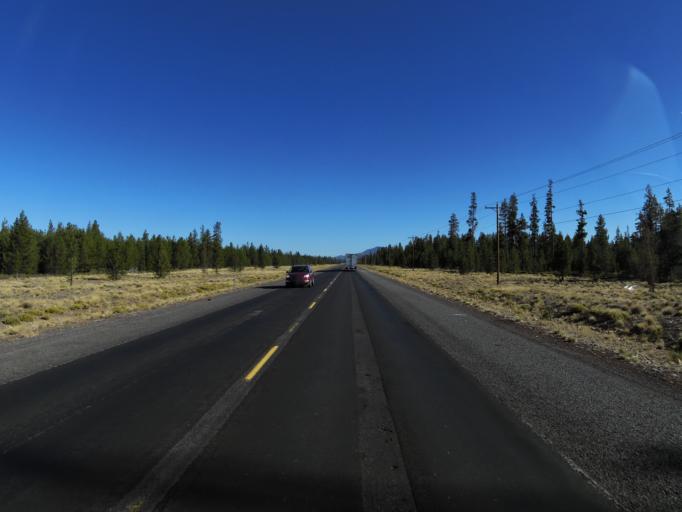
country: US
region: Oregon
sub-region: Deschutes County
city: La Pine
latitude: 43.1481
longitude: -121.7972
